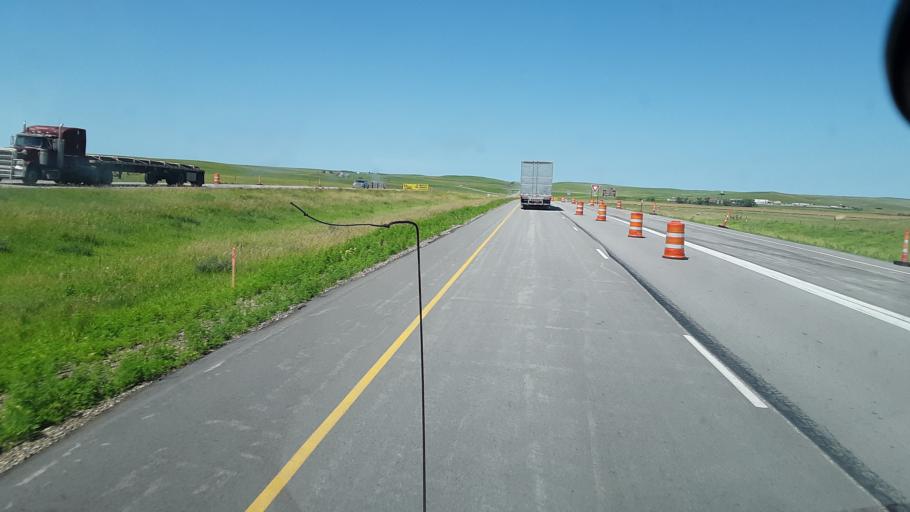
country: US
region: South Dakota
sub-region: Jones County
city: Murdo
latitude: 43.9129
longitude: -100.2923
